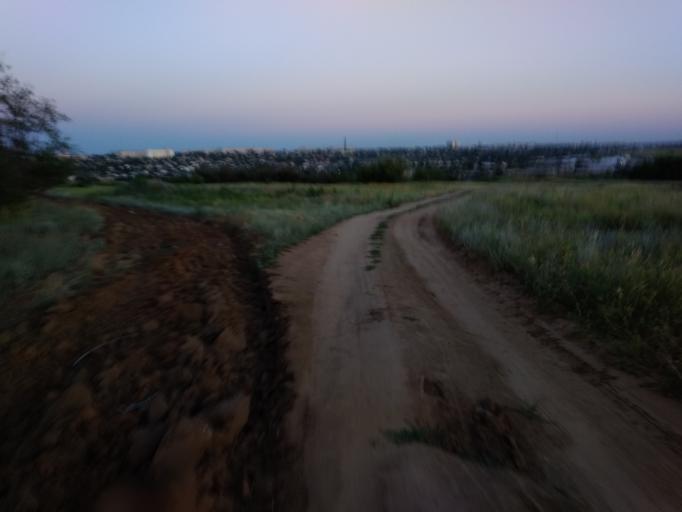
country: RU
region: Volgograd
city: Vodstroy
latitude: 48.8052
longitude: 44.5378
